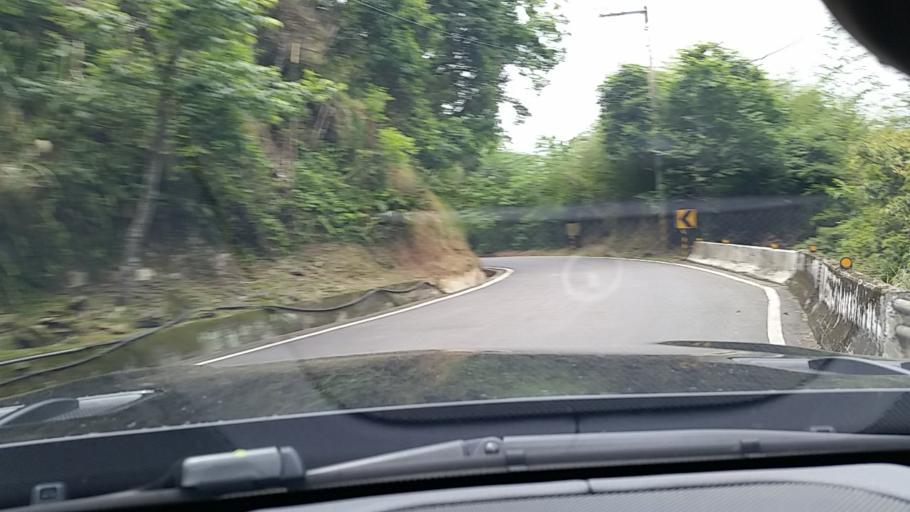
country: TW
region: Taiwan
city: Daxi
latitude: 24.7974
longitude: 121.3165
